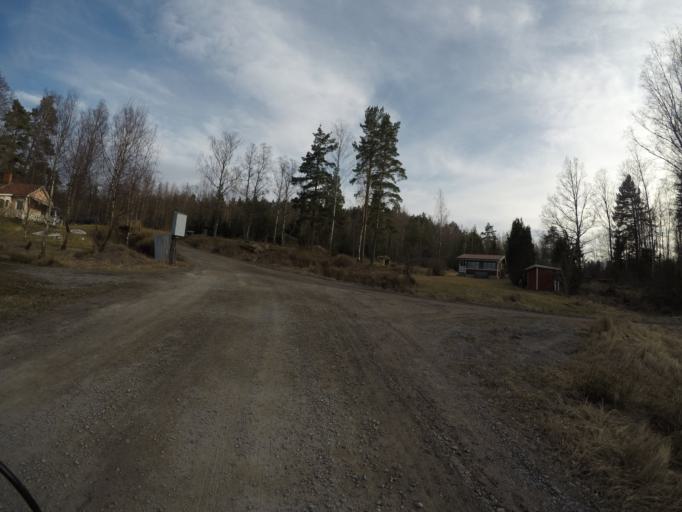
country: SE
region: Soedermanland
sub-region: Eskilstuna Kommun
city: Hallbybrunn
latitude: 59.4287
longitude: 16.4182
